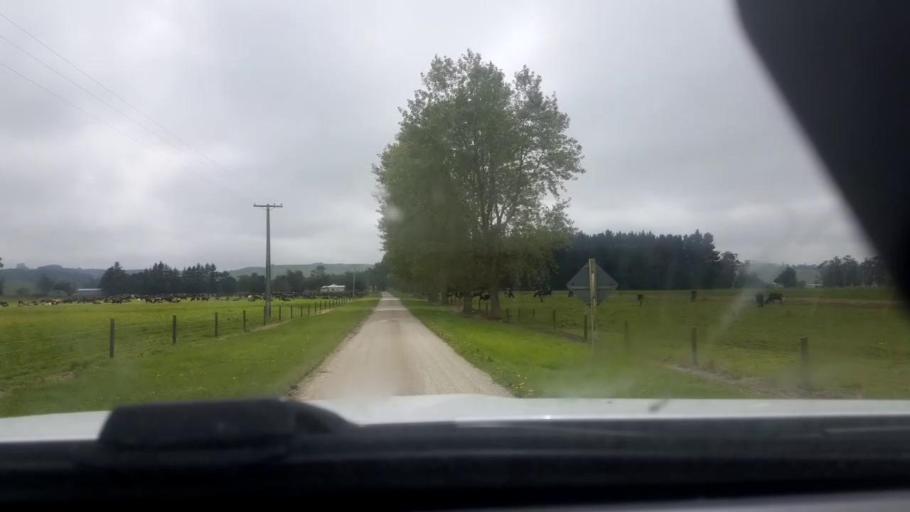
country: NZ
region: Canterbury
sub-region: Timaru District
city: Pleasant Point
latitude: -44.2105
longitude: 171.1107
